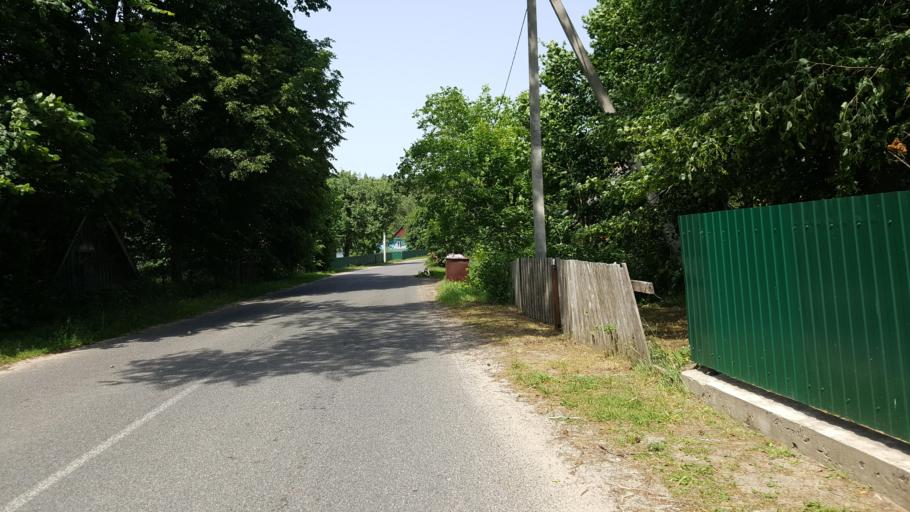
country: BY
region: Brest
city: Kamyanyuki
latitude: 52.5093
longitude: 23.8524
